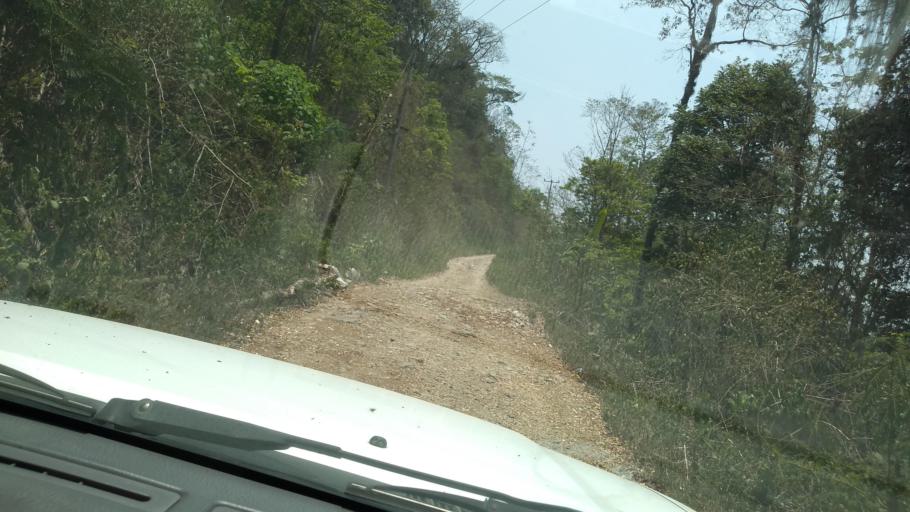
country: MX
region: Veracruz
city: Motzorongo
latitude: 18.5964
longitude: -96.7332
